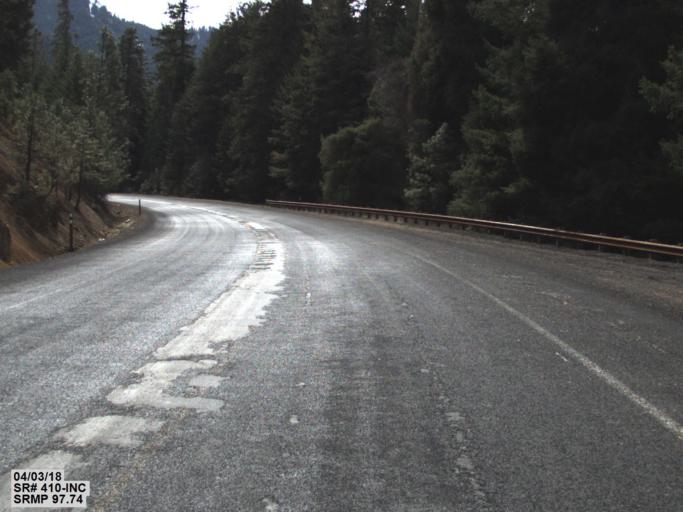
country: US
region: Washington
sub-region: Kittitas County
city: Cle Elum
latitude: 46.9235
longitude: -121.0471
